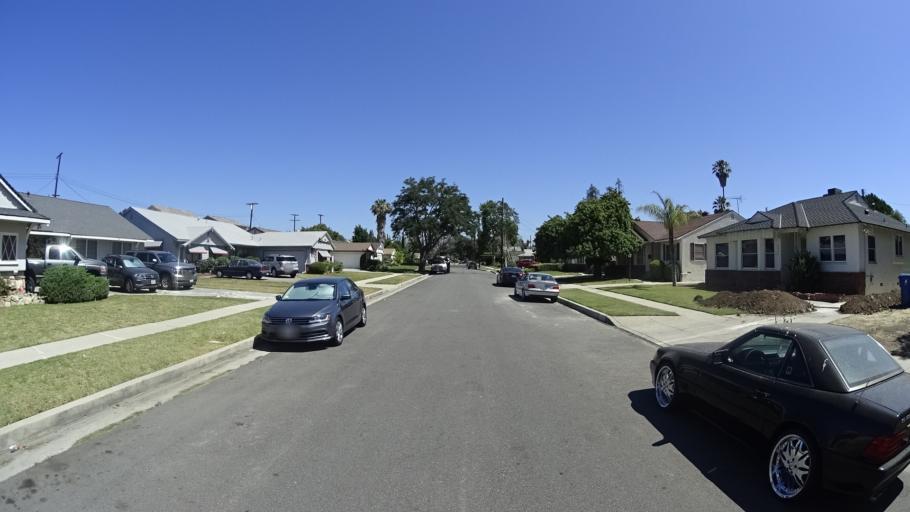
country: US
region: California
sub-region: Los Angeles County
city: Northridge
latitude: 34.1957
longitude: -118.5000
